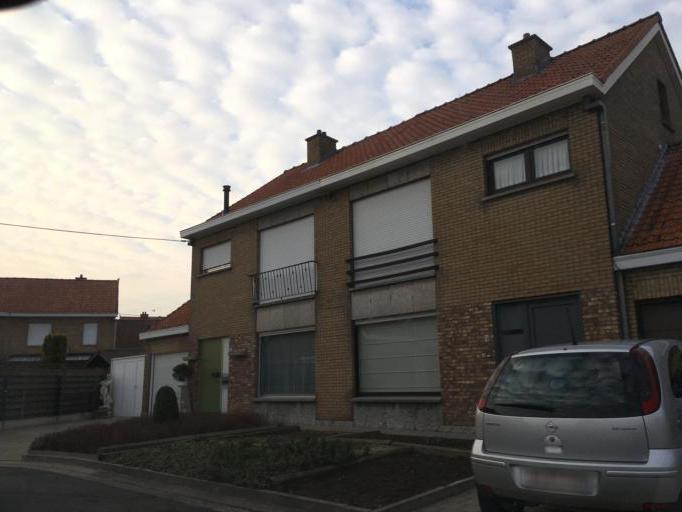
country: BE
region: Flanders
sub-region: Provincie West-Vlaanderen
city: Roeselare
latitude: 50.9344
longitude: 3.1365
